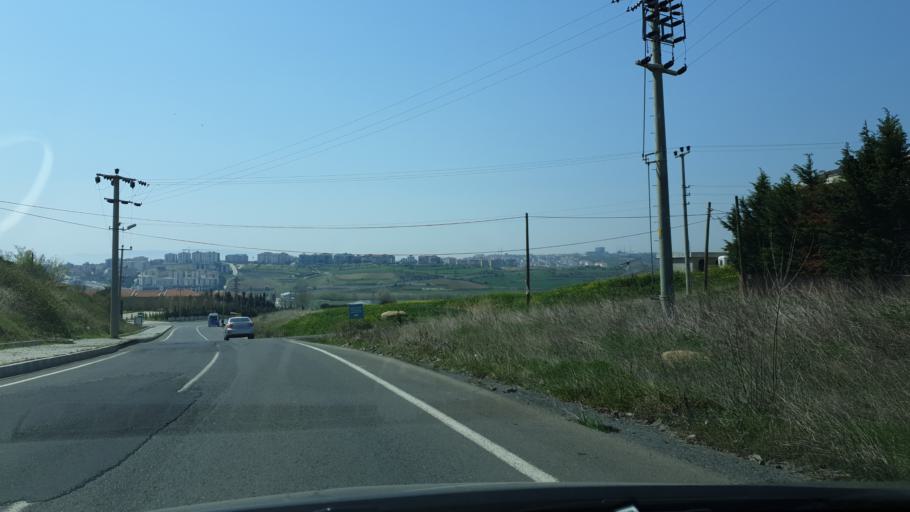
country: TR
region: Tekirdag
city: Tekirdag
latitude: 40.9969
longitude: 27.5829
